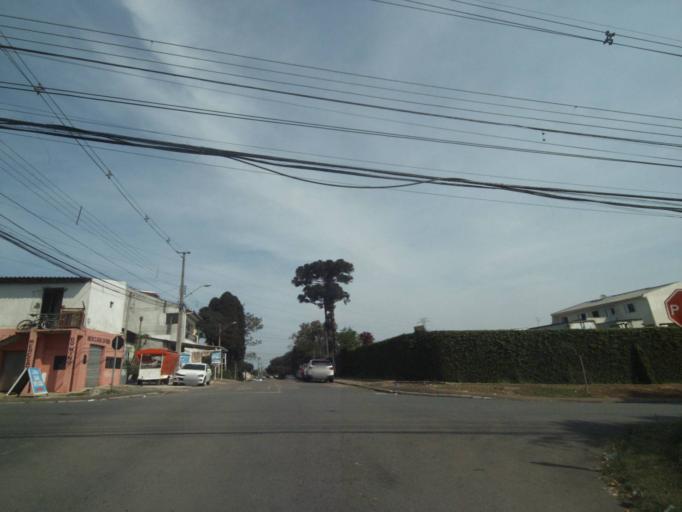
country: BR
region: Parana
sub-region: Curitiba
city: Curitiba
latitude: -25.4633
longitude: -49.3143
